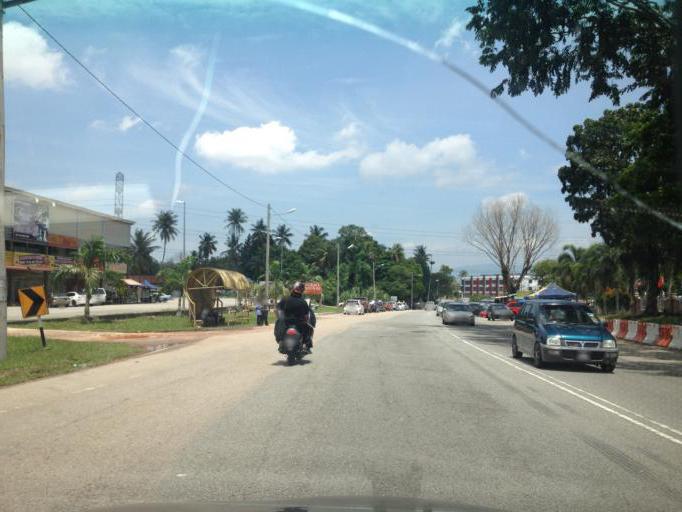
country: MY
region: Kedah
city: Sungai Petani
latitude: 5.6260
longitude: 100.5290
